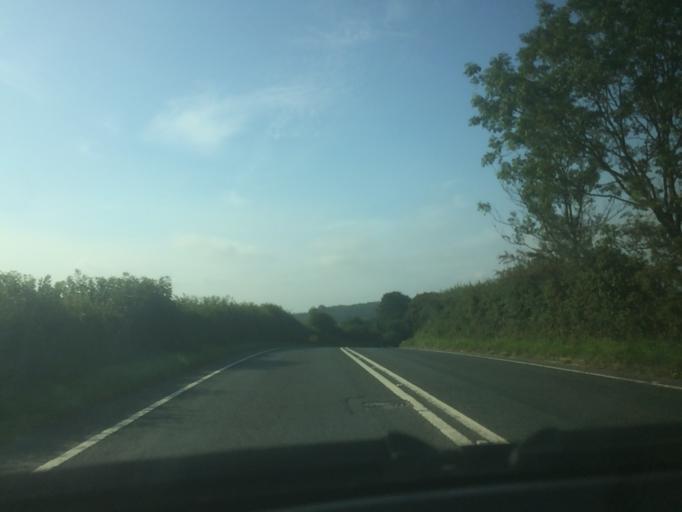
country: GB
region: England
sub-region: Cornwall
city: Pillaton
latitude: 50.4488
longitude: -4.2555
